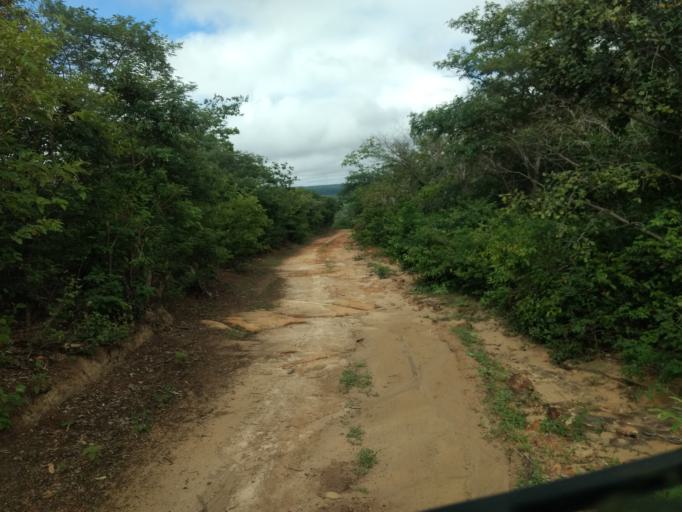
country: BR
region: Ceara
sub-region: Crateus
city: Crateus
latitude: -5.1919
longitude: -40.9489
